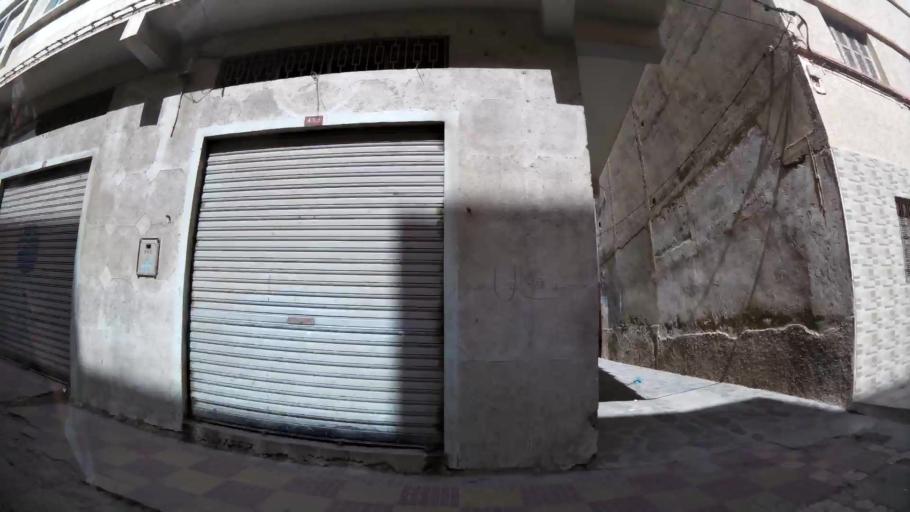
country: MA
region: Oriental
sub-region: Nador
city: Nador
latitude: 35.1683
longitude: -2.9286
